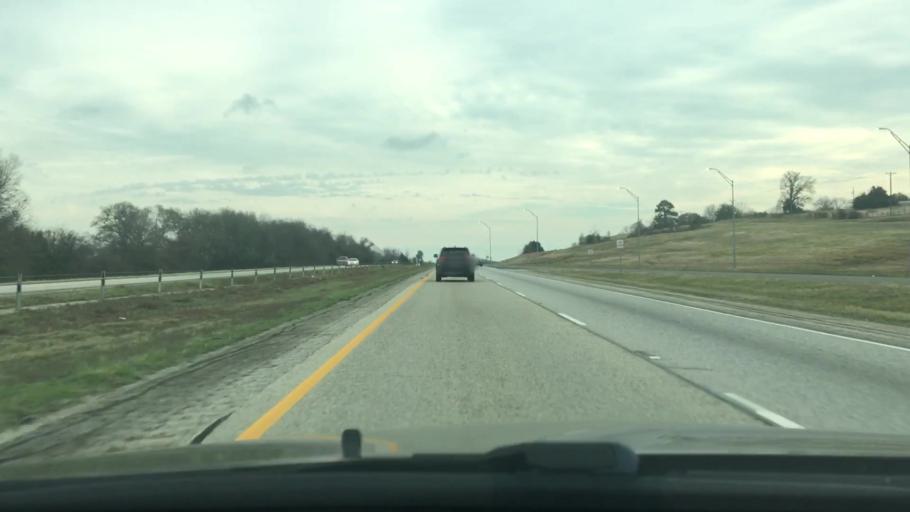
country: US
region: Texas
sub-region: Leon County
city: Centerville
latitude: 31.2785
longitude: -95.9902
